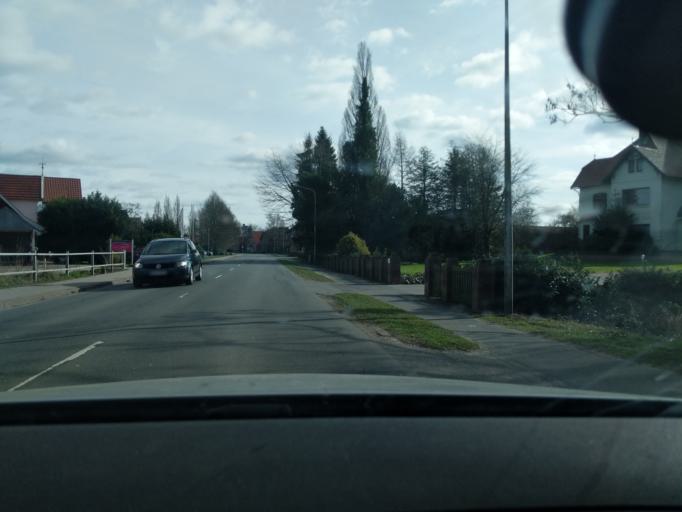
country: DE
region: Lower Saxony
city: Drochtersen
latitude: 53.7146
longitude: 9.3743
